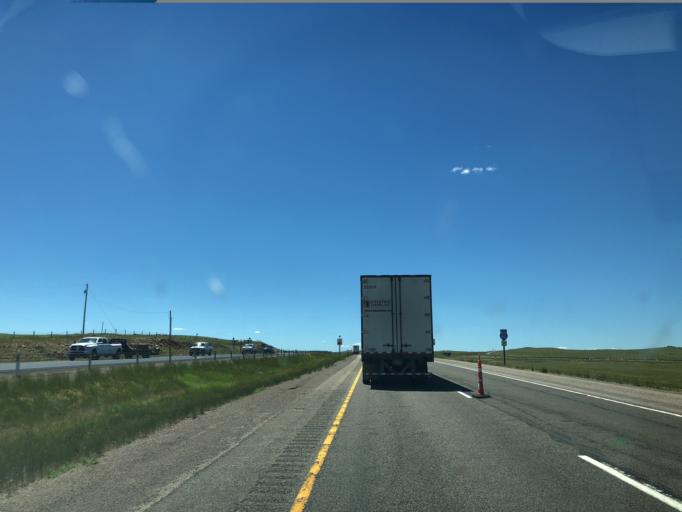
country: US
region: Wyoming
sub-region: Laramie County
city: Cheyenne
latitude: 41.0964
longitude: -105.1882
